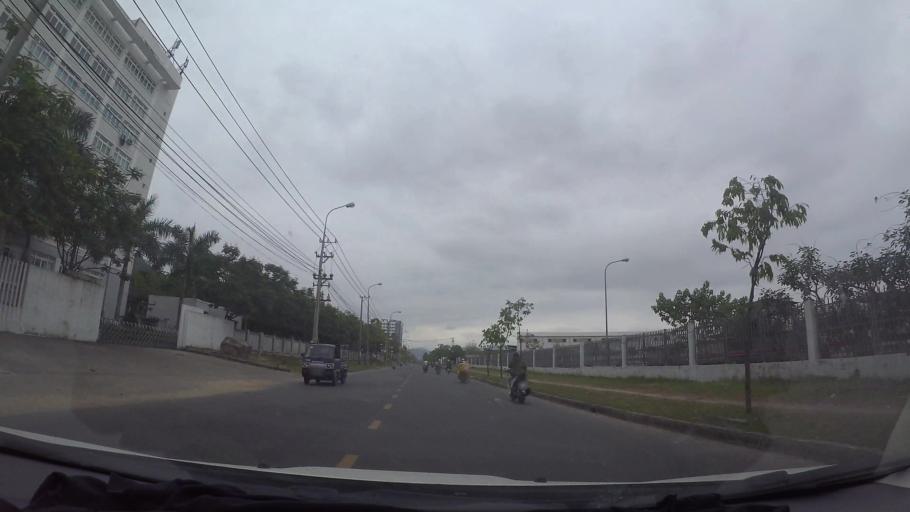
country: VN
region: Da Nang
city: Lien Chieu
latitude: 16.0727
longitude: 108.1397
